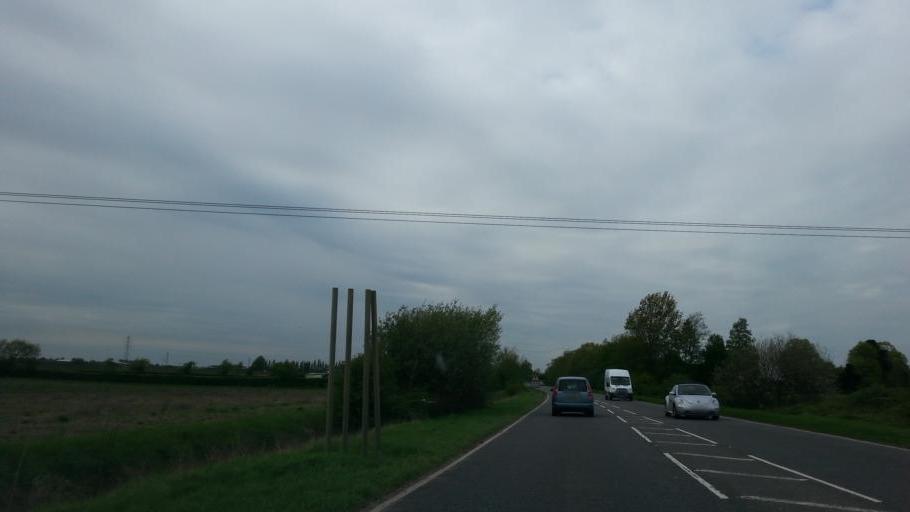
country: GB
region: England
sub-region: Cambridgeshire
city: March
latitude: 52.5466
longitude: 0.0704
